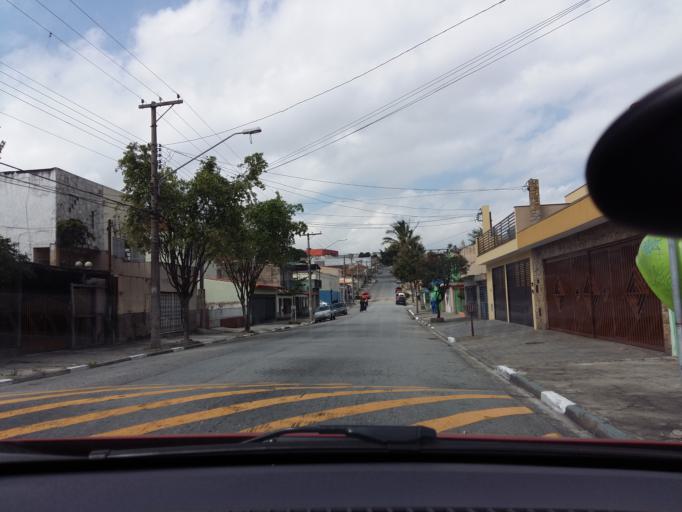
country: BR
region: Sao Paulo
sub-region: Sao Caetano Do Sul
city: Sao Caetano do Sul
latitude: -23.6019
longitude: -46.5646
